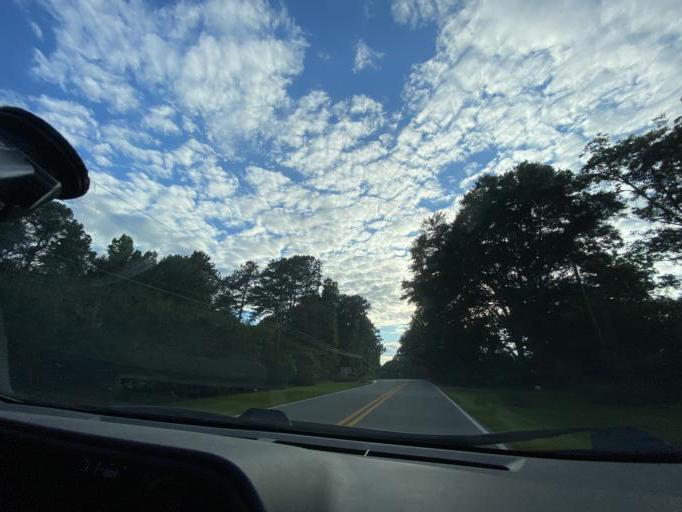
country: US
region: Georgia
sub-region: Fayette County
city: Peachtree City
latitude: 33.4119
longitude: -84.6602
